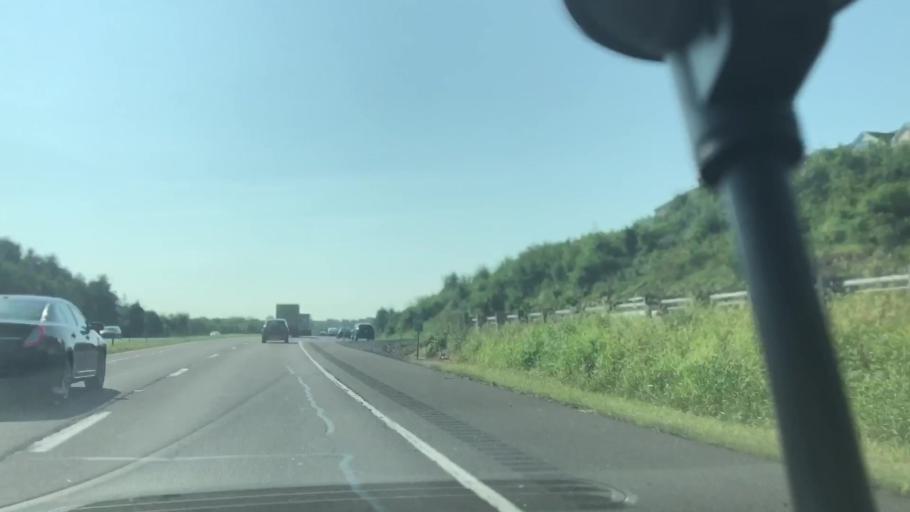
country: US
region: Pennsylvania
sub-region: Montgomery County
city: Royersford
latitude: 40.1941
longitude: -75.5235
